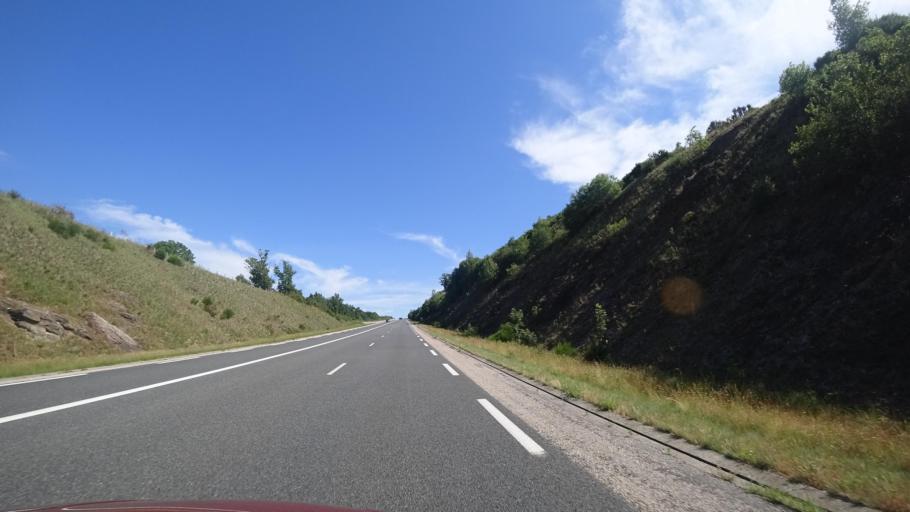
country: FR
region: Midi-Pyrenees
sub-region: Departement de l'Aveyron
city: Pont-de-Salars
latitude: 44.2794
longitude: 2.7217
